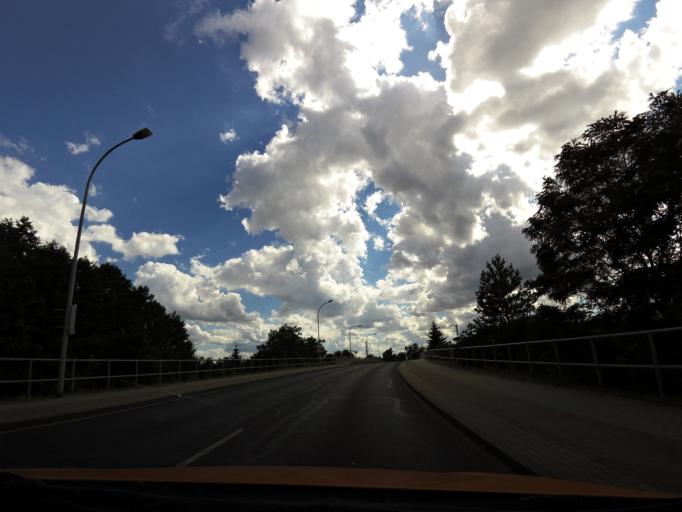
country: DE
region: Brandenburg
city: Konigs Wusterhausen
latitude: 52.3042
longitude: 13.6325
